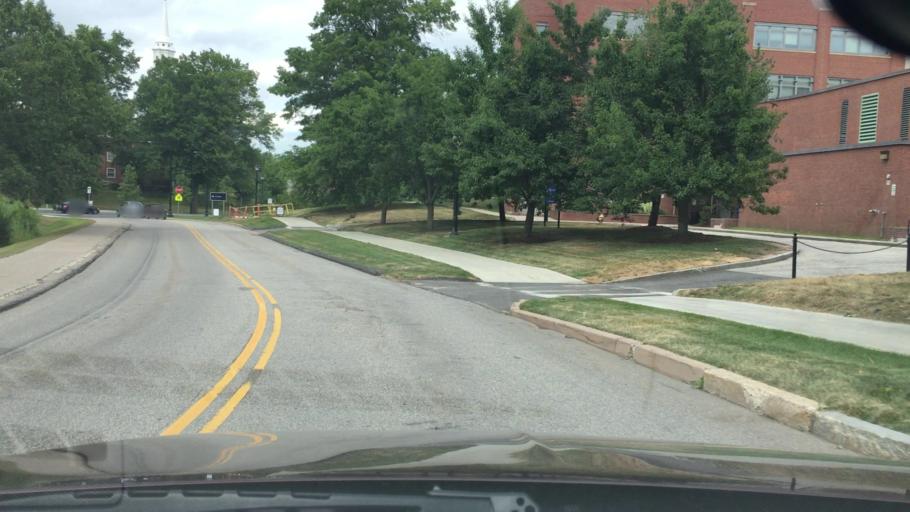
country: US
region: Connecticut
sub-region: Tolland County
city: Storrs
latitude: 41.8105
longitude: -72.2519
